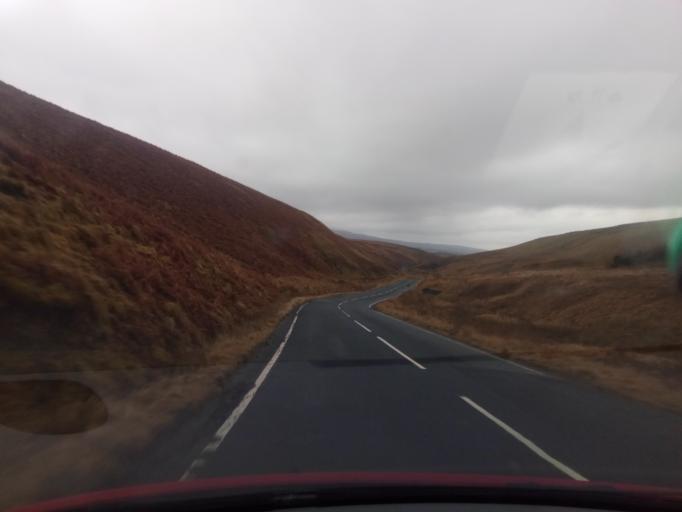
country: GB
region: Scotland
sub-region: The Scottish Borders
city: Hawick
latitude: 55.2887
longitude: -2.6683
